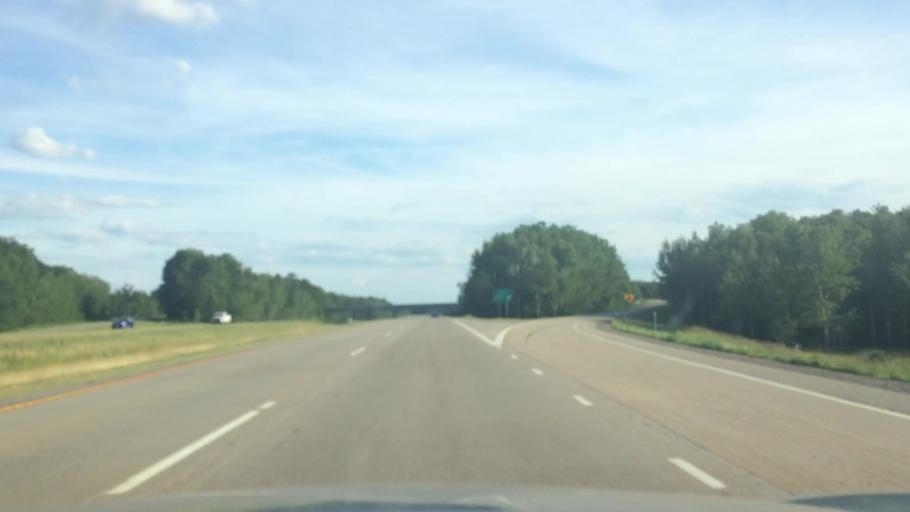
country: US
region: Wisconsin
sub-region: Marathon County
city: Mosinee
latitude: 44.6796
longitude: -89.6419
